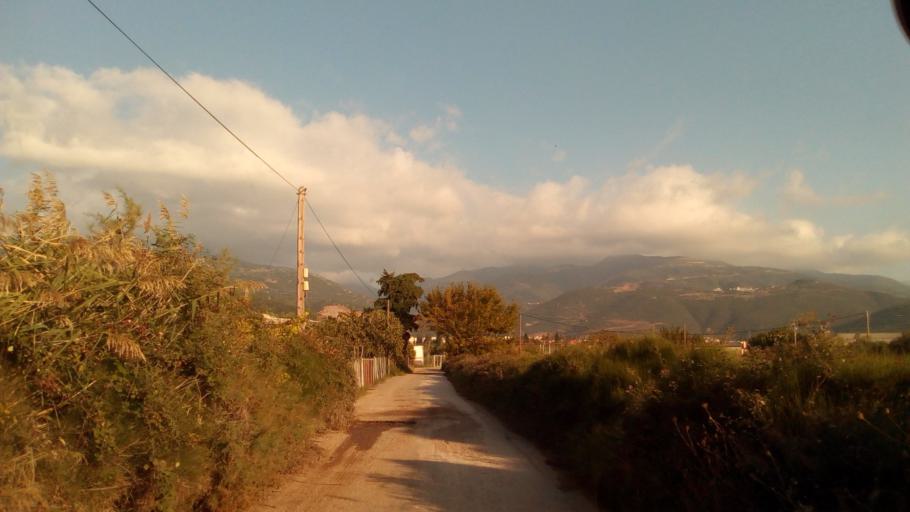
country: GR
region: West Greece
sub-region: Nomos Aitolias kai Akarnanias
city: Nafpaktos
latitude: 38.3861
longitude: 21.8499
